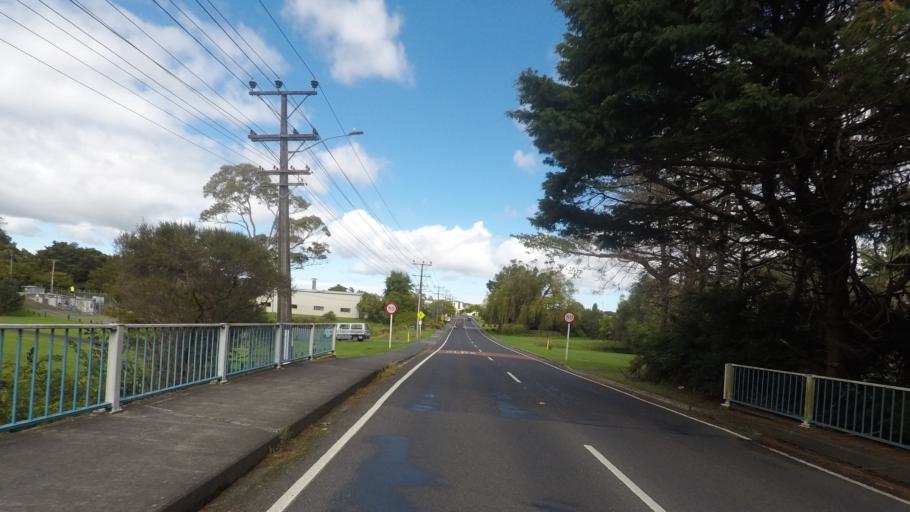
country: NZ
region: Auckland
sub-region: Auckland
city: Muriwai Beach
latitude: -36.7704
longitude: 174.5492
